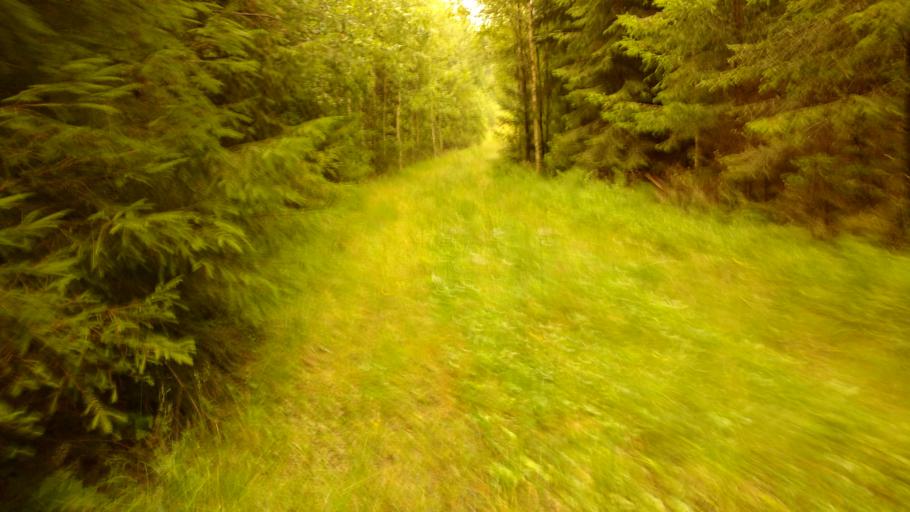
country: FI
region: Varsinais-Suomi
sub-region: Salo
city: Pertteli
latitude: 60.4076
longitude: 23.2337
